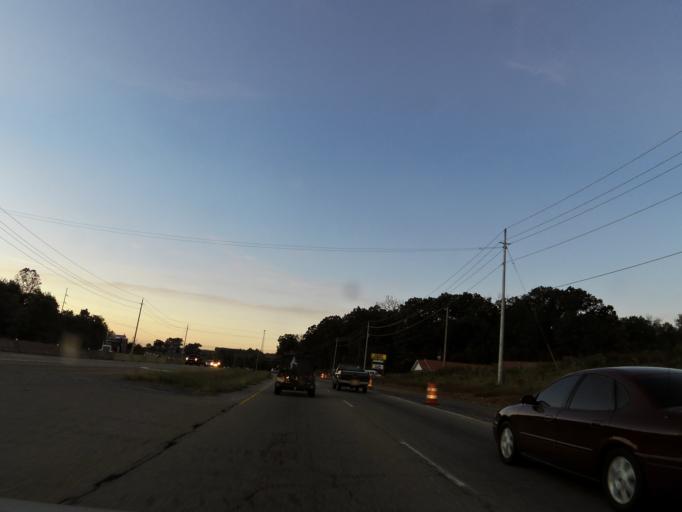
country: US
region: Tennessee
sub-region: Sevier County
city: Sevierville
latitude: 35.9454
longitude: -83.5840
